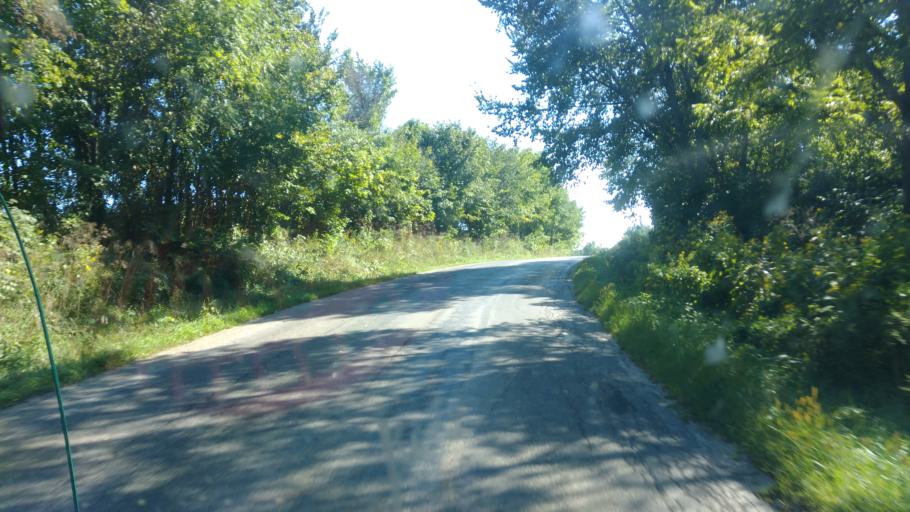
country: US
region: Ohio
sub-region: Ashland County
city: Ashland
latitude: 40.9108
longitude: -82.4354
